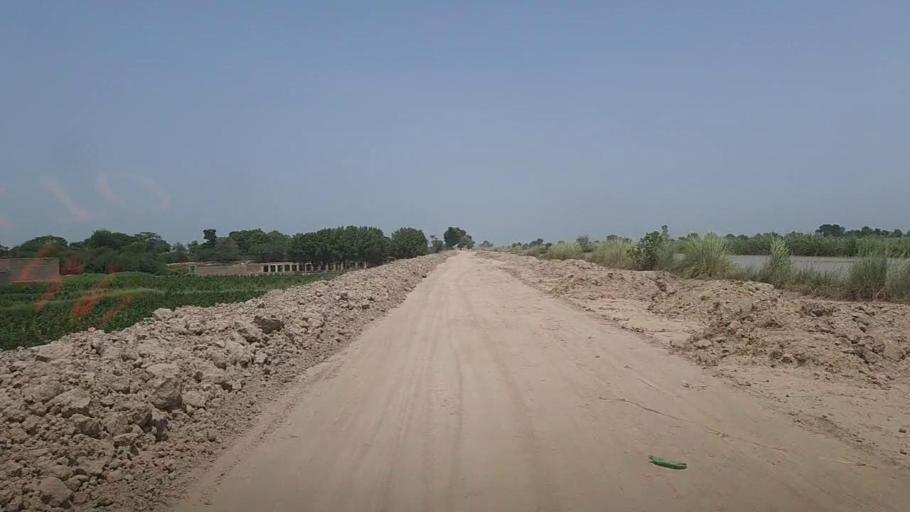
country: PK
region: Sindh
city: Pad Idan
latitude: 26.7894
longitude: 68.2764
